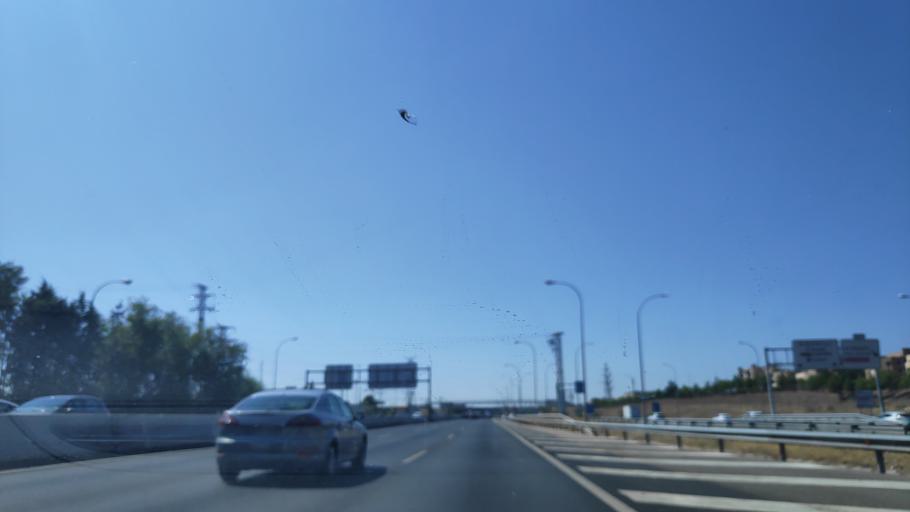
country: ES
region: Madrid
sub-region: Provincia de Madrid
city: Getafe
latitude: 40.3270
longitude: -3.7268
